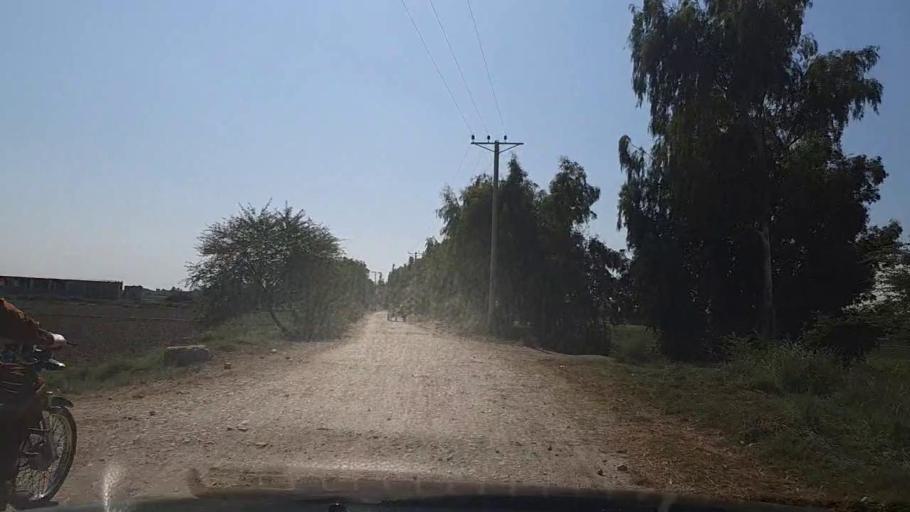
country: PK
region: Sindh
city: Mirpur Sakro
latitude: 24.5977
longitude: 67.7832
